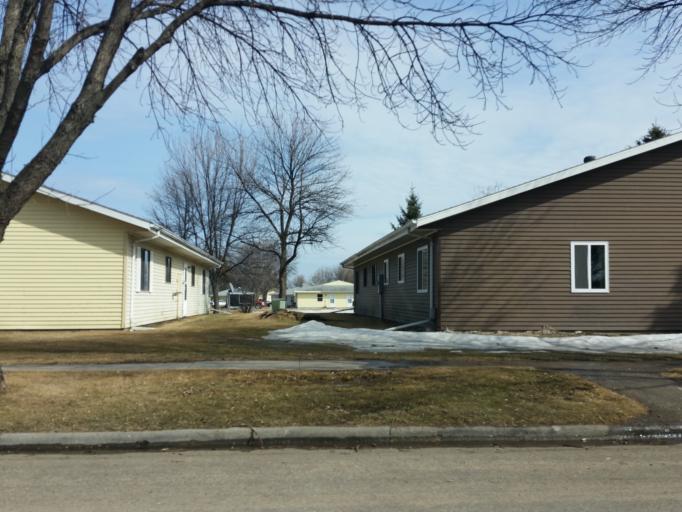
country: US
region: North Dakota
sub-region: Walsh County
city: Grafton
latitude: 48.4147
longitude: -97.4025
